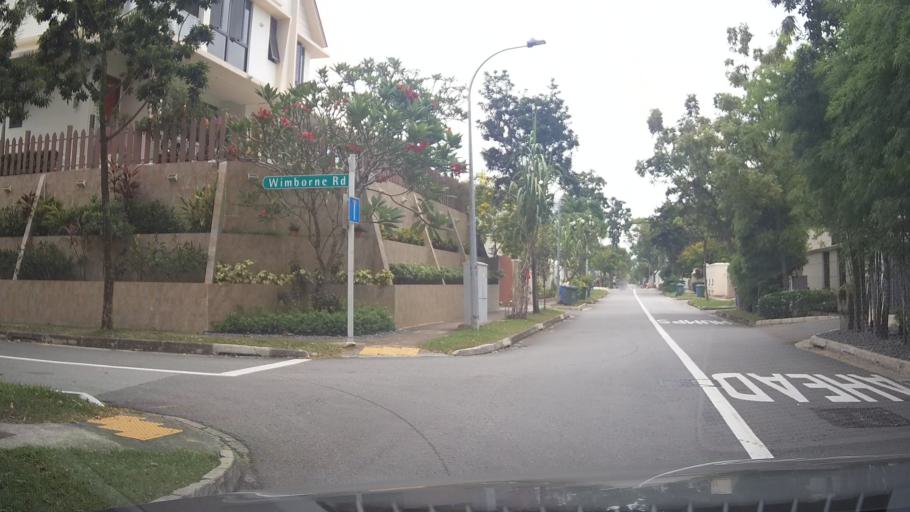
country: SG
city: Singapore
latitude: 1.3041
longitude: 103.8859
